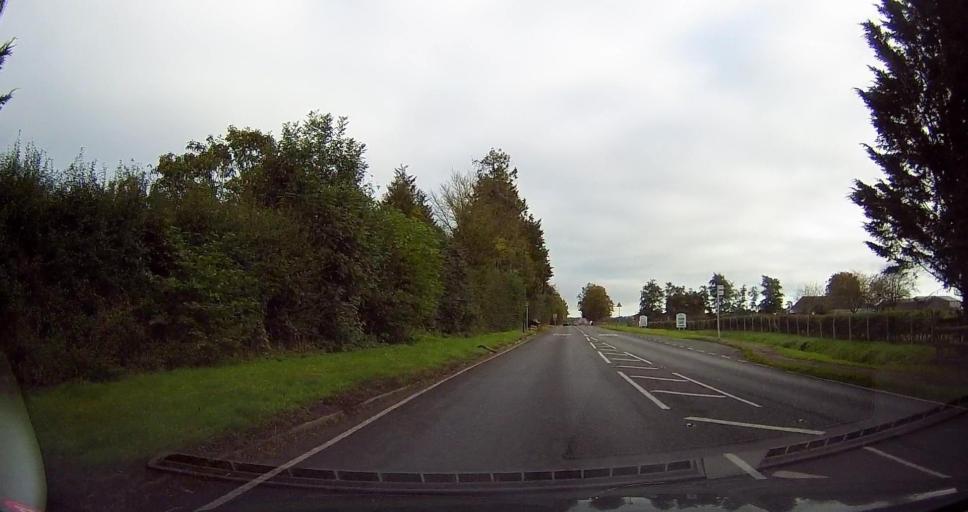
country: GB
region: England
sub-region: Kent
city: Hadlow
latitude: 51.2168
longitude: 0.3129
